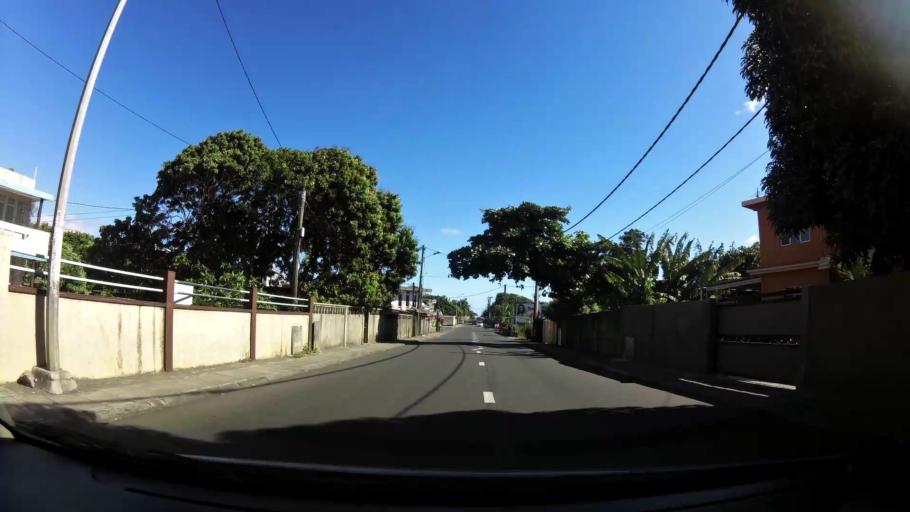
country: MU
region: Plaines Wilhems
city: Quatre Bornes
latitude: -20.2783
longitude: 57.4598
